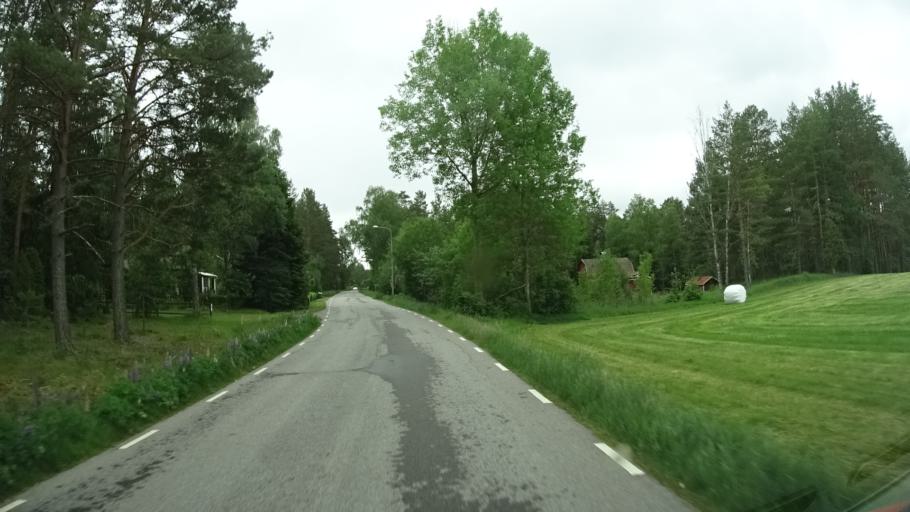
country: SE
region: Joenkoeping
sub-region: Eksjo Kommun
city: Mariannelund
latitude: 57.6950
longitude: 15.6246
